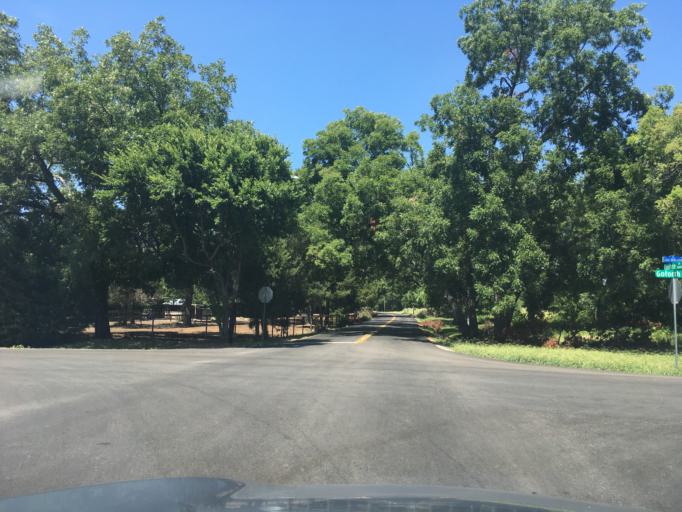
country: US
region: Texas
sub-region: Dallas County
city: Highland Park
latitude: 32.8605
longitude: -96.7290
